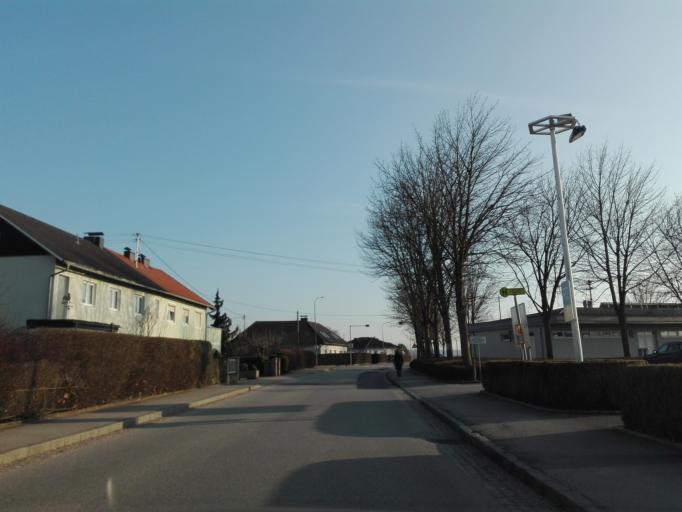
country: AT
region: Upper Austria
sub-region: Politischer Bezirk Linz-Land
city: Horsching
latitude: 48.2220
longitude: 14.1789
